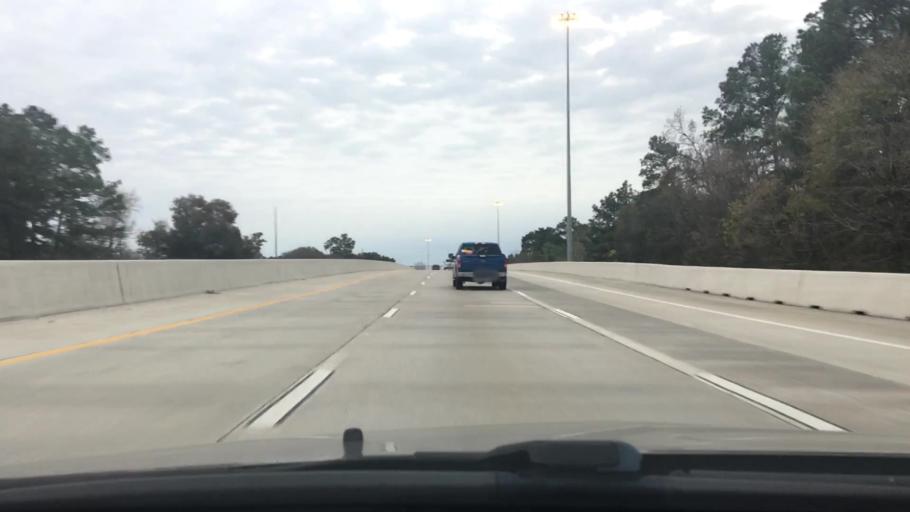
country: US
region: Texas
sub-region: Harris County
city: Spring
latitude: 30.0776
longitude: -95.4111
